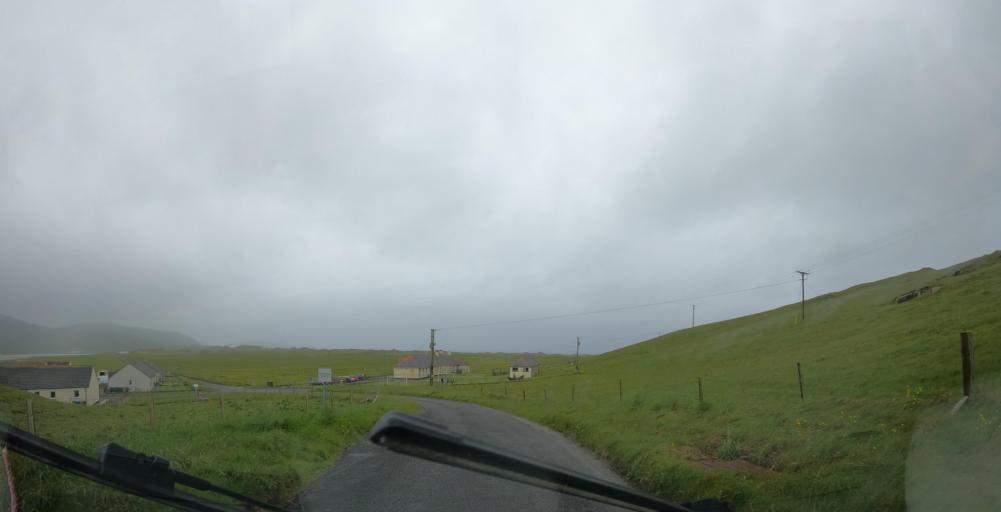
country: GB
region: Scotland
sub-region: Eilean Siar
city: Barra
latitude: 57.0340
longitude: -7.4339
